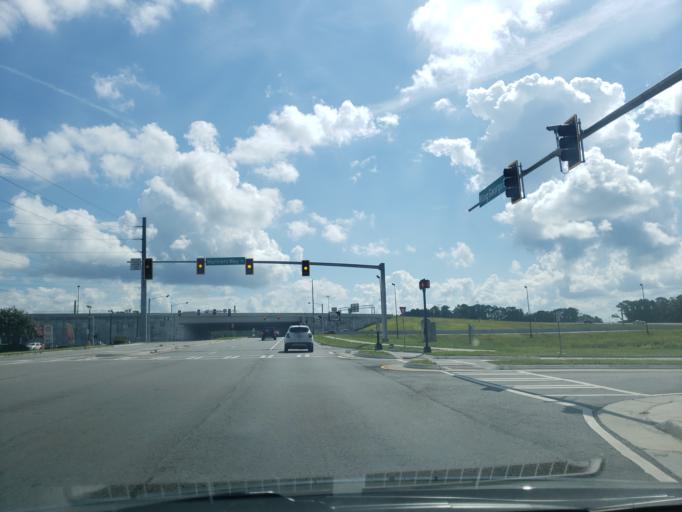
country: US
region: Georgia
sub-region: Chatham County
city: Georgetown
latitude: 31.9849
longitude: -81.2194
